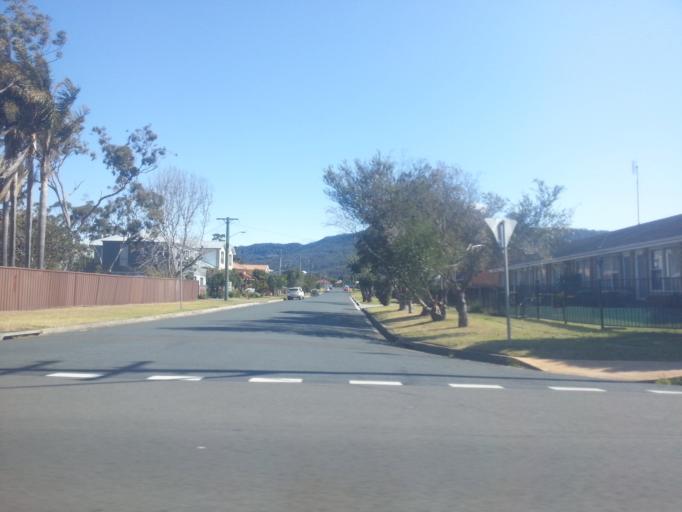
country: AU
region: New South Wales
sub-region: Wollongong
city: East Corrimal
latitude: -34.3734
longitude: 150.9093
